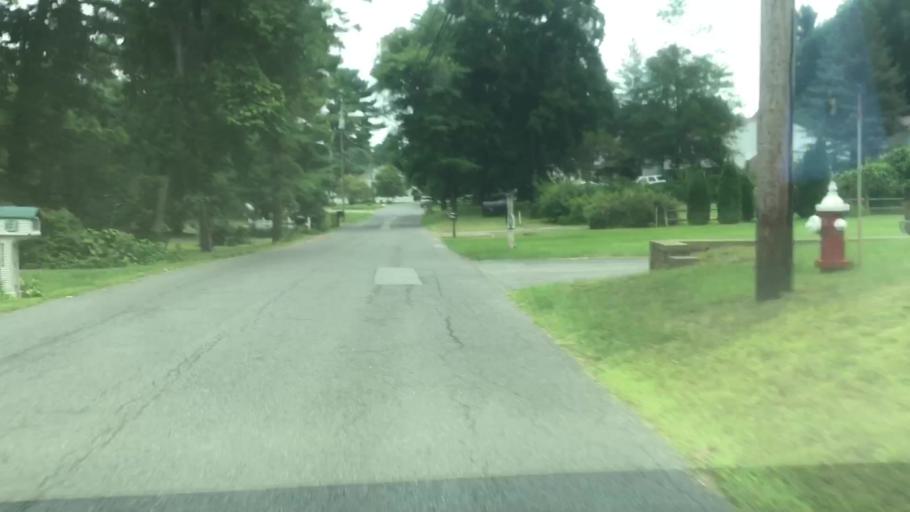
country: US
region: New York
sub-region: Albany County
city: Westmere
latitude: 42.7312
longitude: -73.9250
